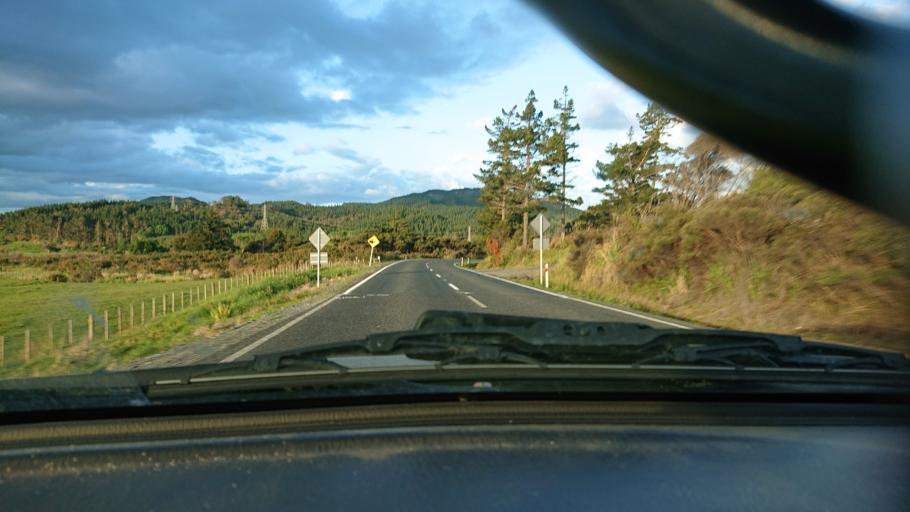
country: NZ
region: Auckland
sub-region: Auckland
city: Parakai
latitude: -36.5111
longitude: 174.4529
